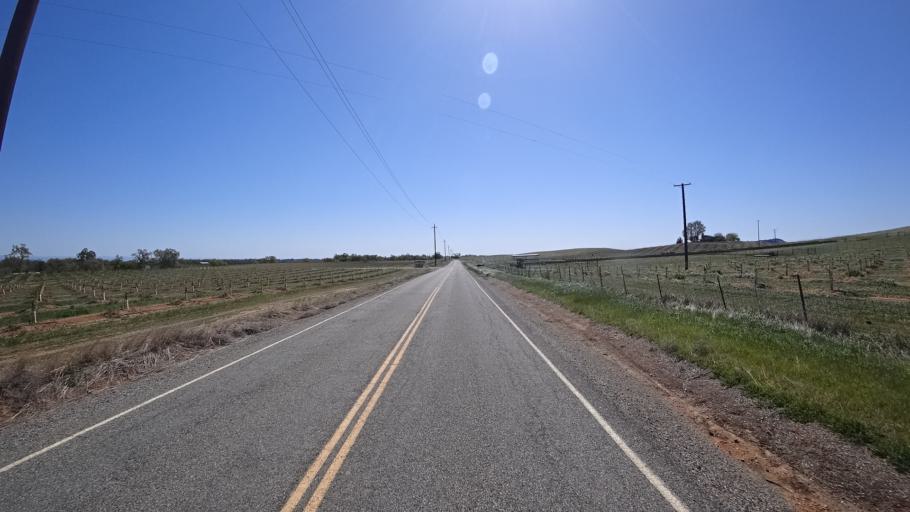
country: US
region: California
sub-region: Glenn County
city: Orland
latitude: 39.8039
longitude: -122.3266
